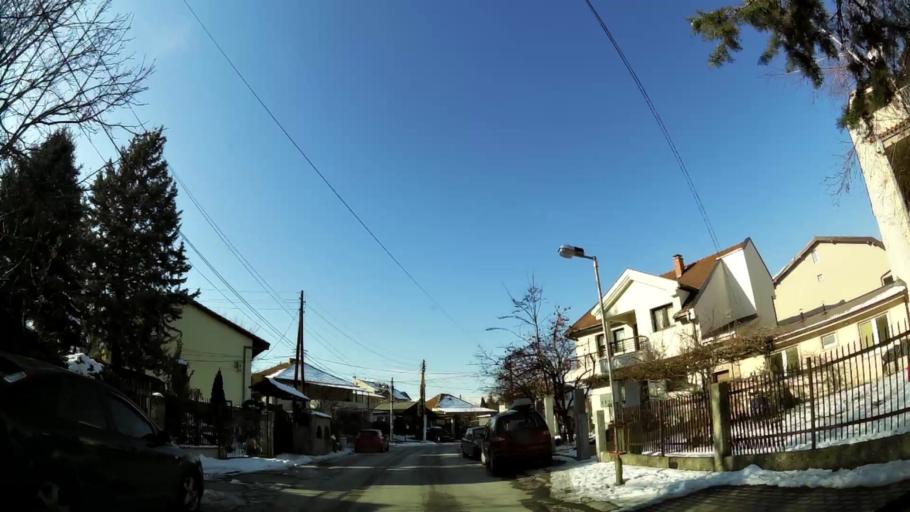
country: MK
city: Krushopek
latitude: 42.0007
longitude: 21.3796
